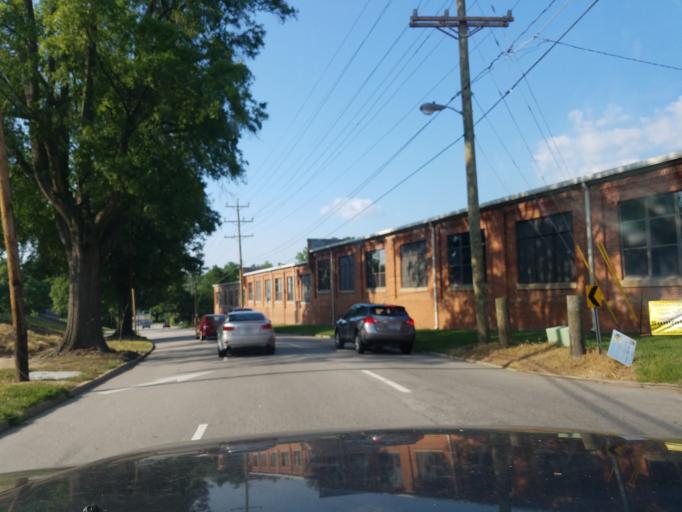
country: US
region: North Carolina
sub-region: Durham County
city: Durham
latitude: 36.0034
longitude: -78.9057
